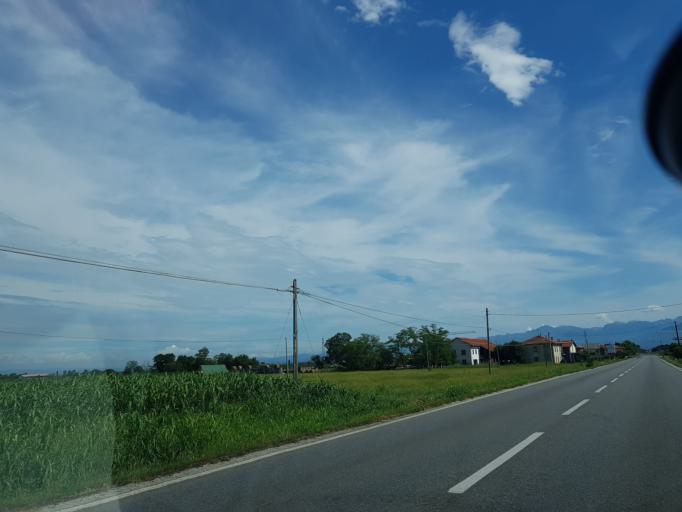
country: IT
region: Piedmont
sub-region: Provincia di Cuneo
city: Busca
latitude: 44.4947
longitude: 7.4954
